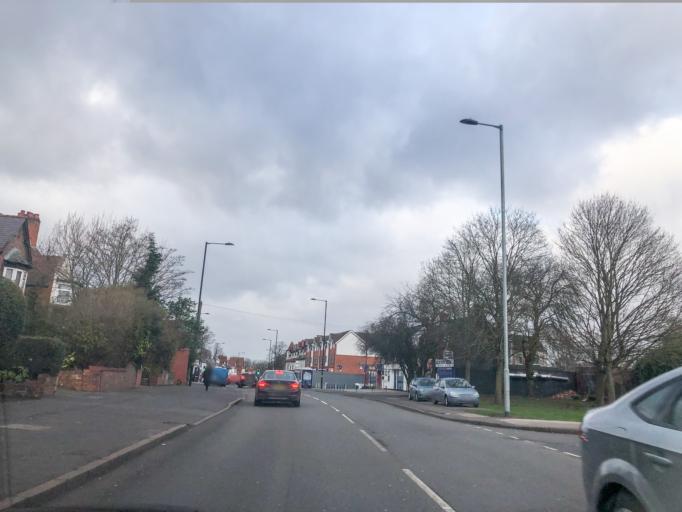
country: GB
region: England
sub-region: Solihull
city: Tidbury Green
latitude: 52.4201
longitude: -1.8916
